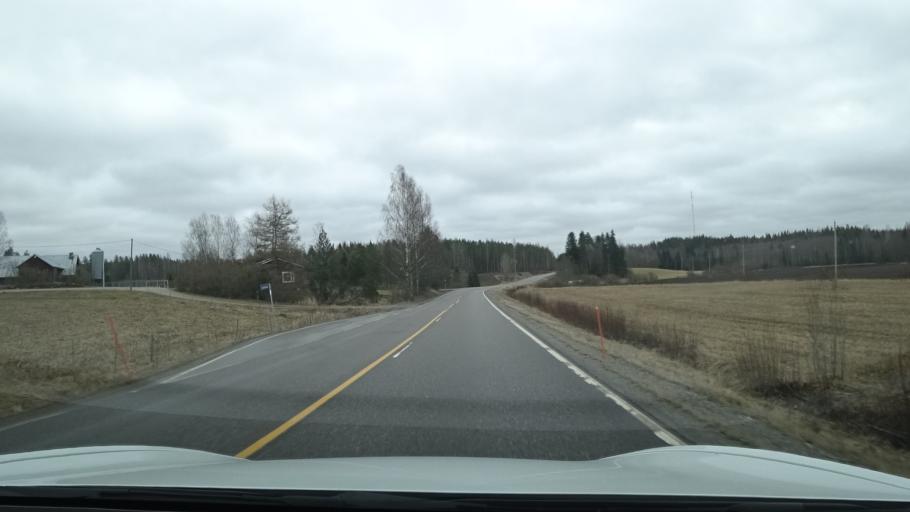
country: FI
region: Uusimaa
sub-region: Helsinki
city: Pornainen
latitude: 60.4867
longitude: 25.4180
